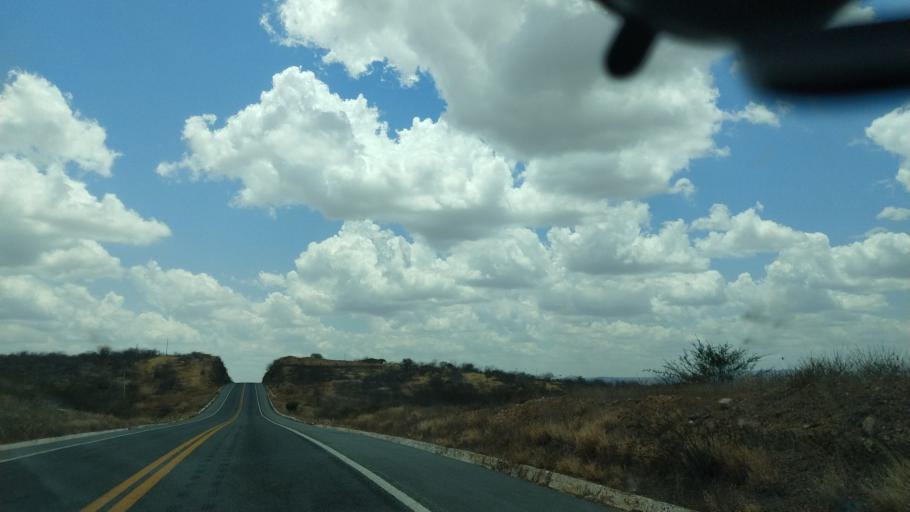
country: BR
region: Rio Grande do Norte
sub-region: Currais Novos
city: Currais Novos
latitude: -6.2555
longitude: -36.4828
